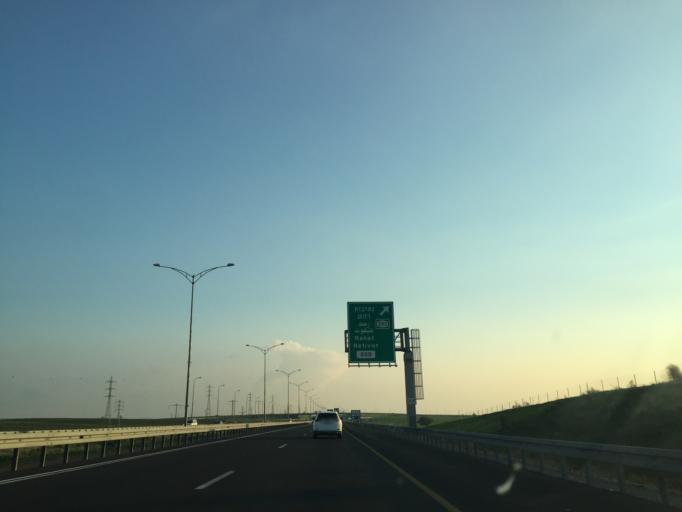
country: IL
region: Southern District
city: Lehavim
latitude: 31.4514
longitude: 34.7705
